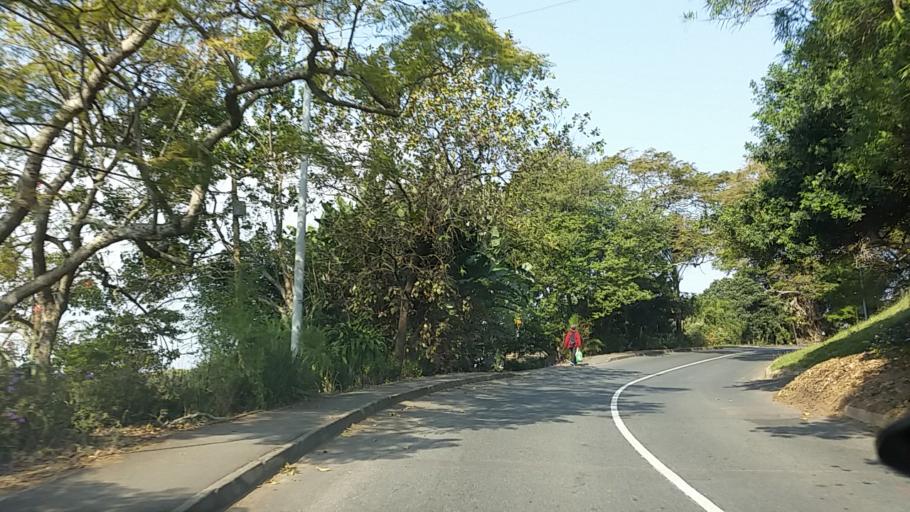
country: ZA
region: KwaZulu-Natal
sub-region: eThekwini Metropolitan Municipality
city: Berea
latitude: -29.8365
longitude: 30.9358
